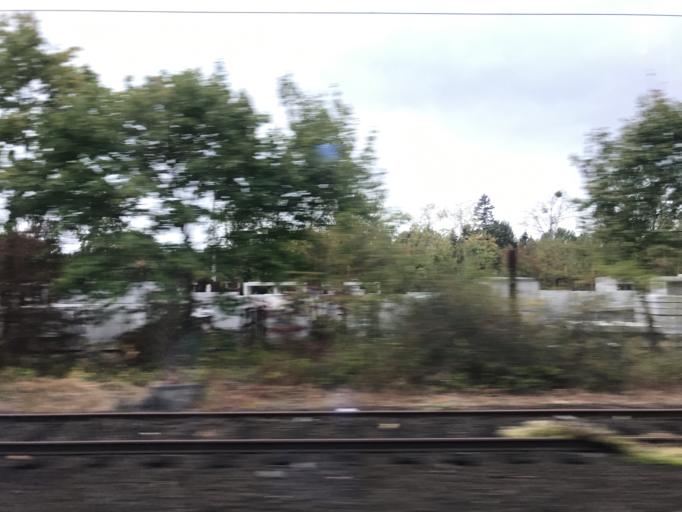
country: DE
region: Hesse
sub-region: Regierungsbezirk Darmstadt
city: Stockstadt am Rhein
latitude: 49.8168
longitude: 8.4775
